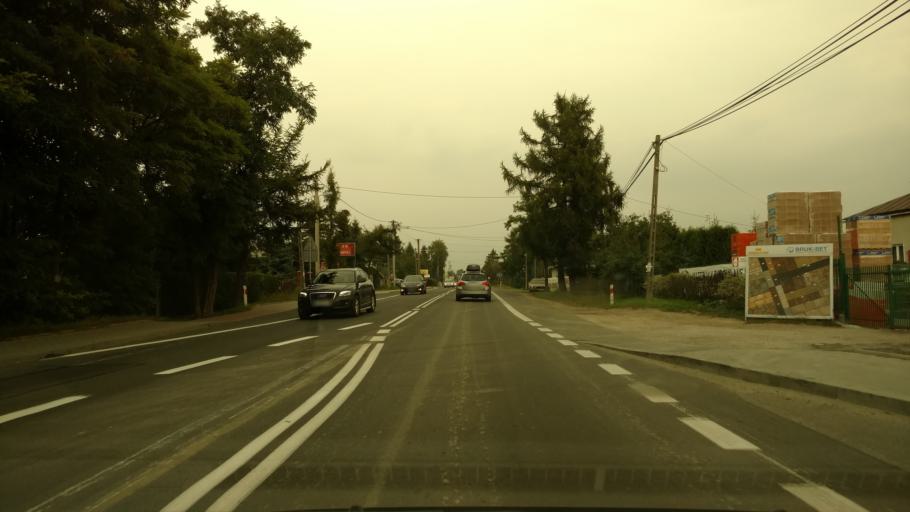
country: PL
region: Lesser Poland Voivodeship
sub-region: Powiat krakowski
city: Michalowice
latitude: 50.1205
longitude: 19.9673
